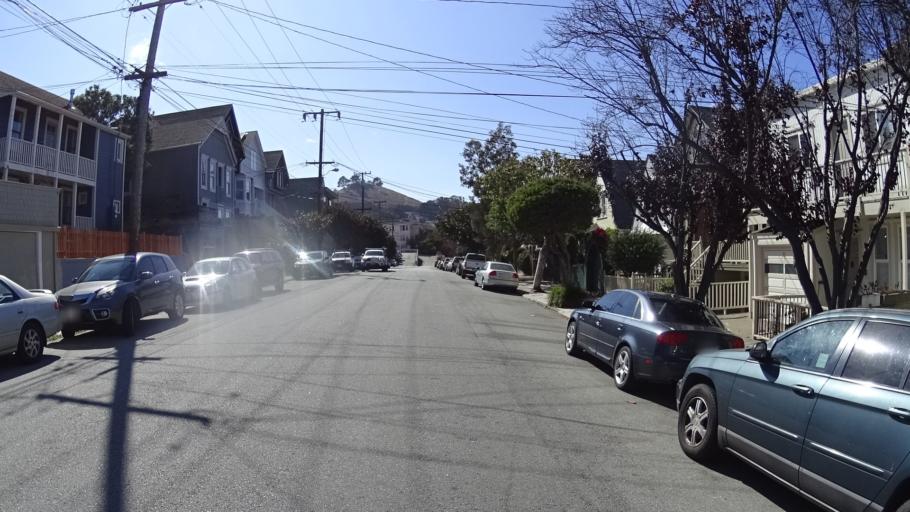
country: US
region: California
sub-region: San Francisco County
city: San Francisco
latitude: 37.7474
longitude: -122.4074
